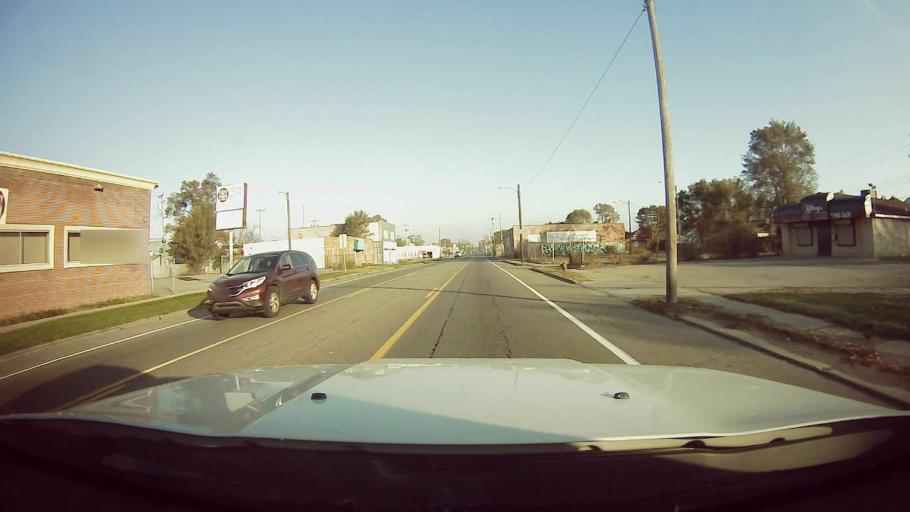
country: US
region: Michigan
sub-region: Oakland County
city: Oak Park
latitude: 42.4284
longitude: -83.1608
